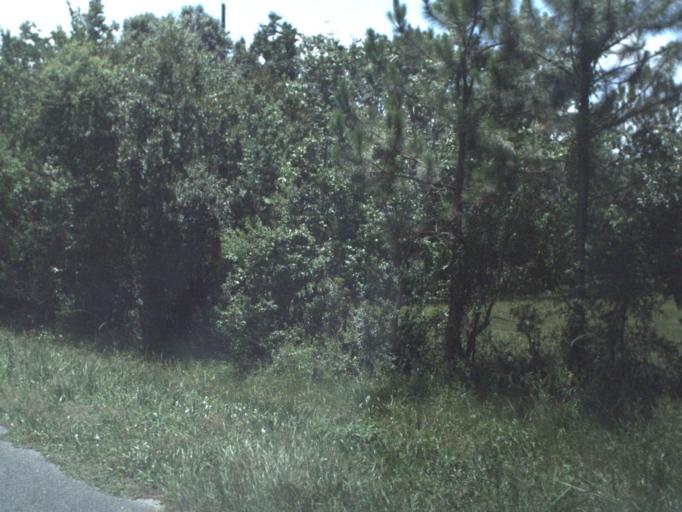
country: US
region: Florida
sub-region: Bradford County
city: Starke
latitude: 29.9718
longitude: -82.1219
